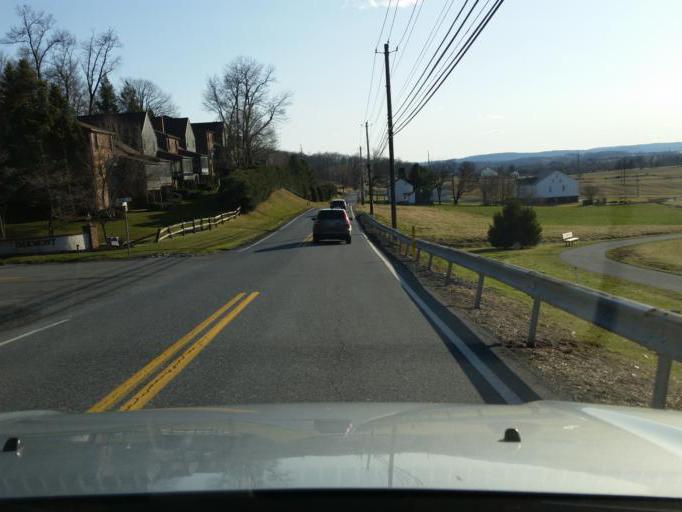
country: US
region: Pennsylvania
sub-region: Dauphin County
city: Hummelstown
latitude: 40.2541
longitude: -76.6907
